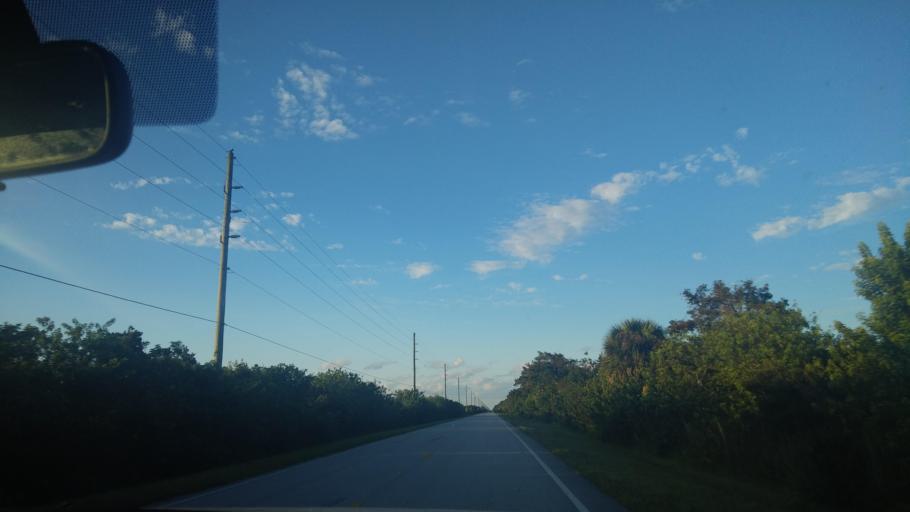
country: US
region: Florida
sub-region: Indian River County
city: Fellsmere
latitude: 27.6679
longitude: -80.6432
